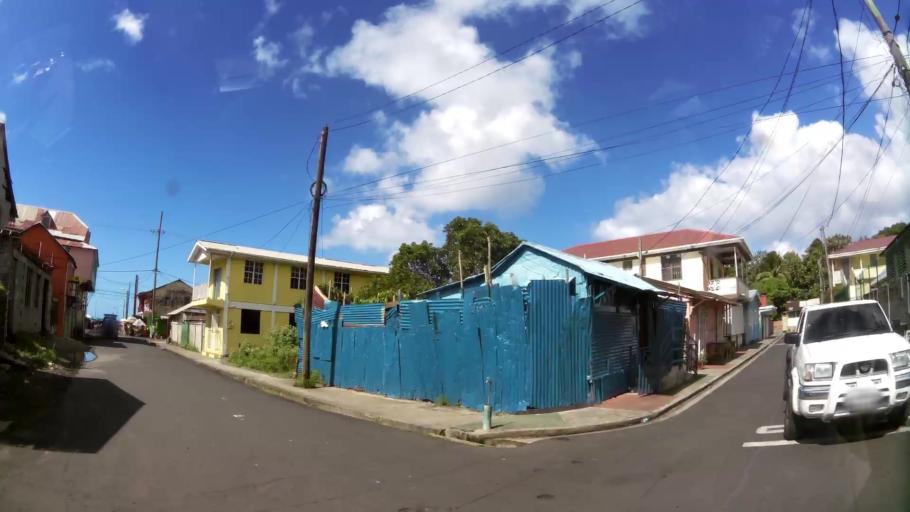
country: DM
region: Saint John
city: Portsmouth
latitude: 15.5773
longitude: -61.4568
